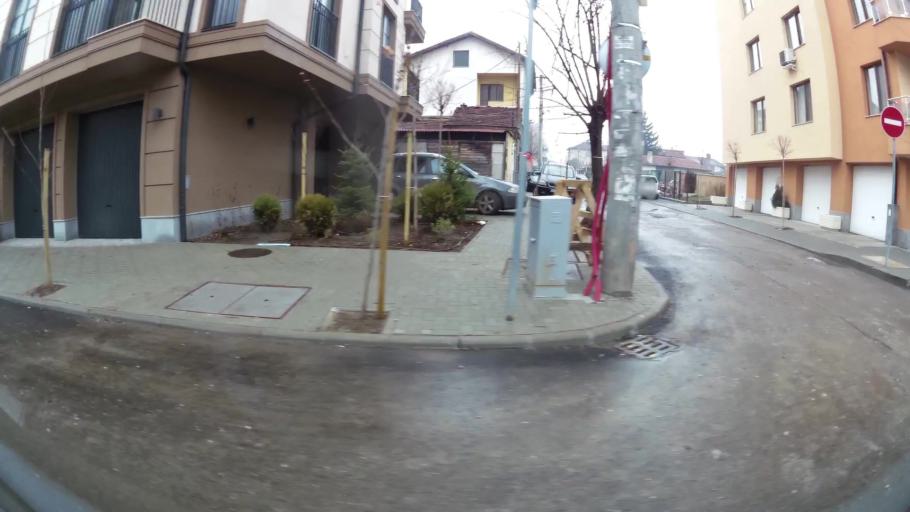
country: BG
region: Sofia-Capital
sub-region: Stolichna Obshtina
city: Sofia
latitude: 42.7311
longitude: 23.2994
